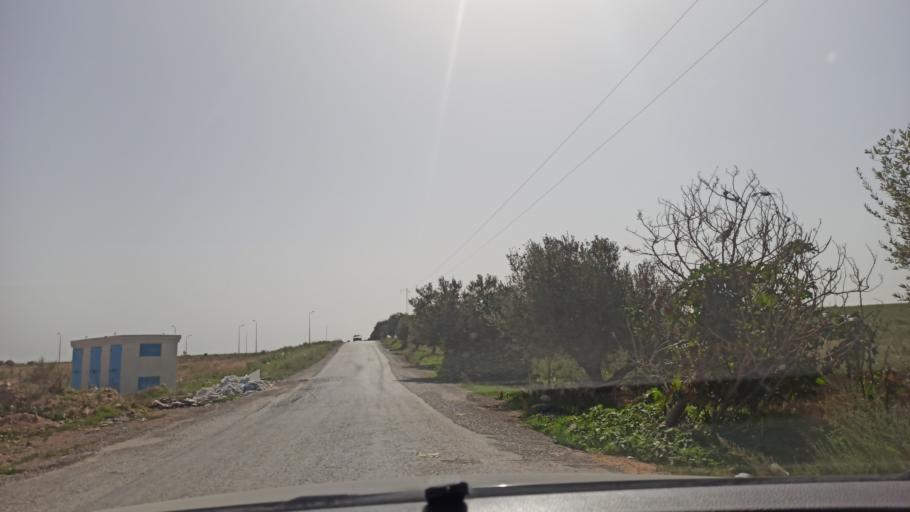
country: TN
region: Manouba
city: Manouba
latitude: 36.7372
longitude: 10.0834
